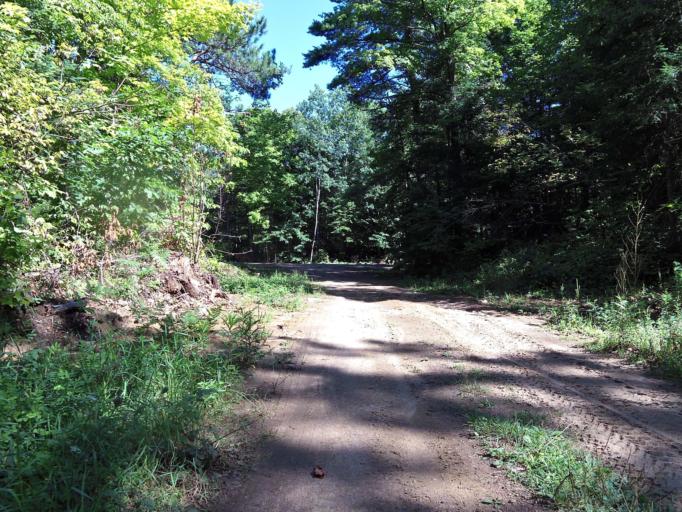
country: CA
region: Ontario
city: Renfrew
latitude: 45.1278
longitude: -76.7269
